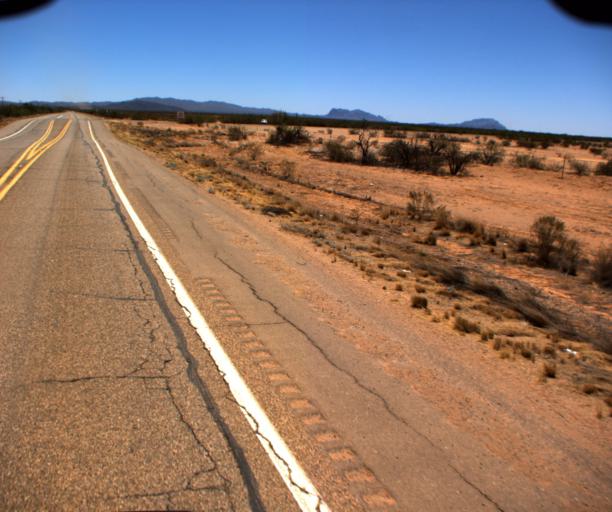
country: US
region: Arizona
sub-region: Pima County
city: Ajo
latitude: 32.1840
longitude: -112.3594
